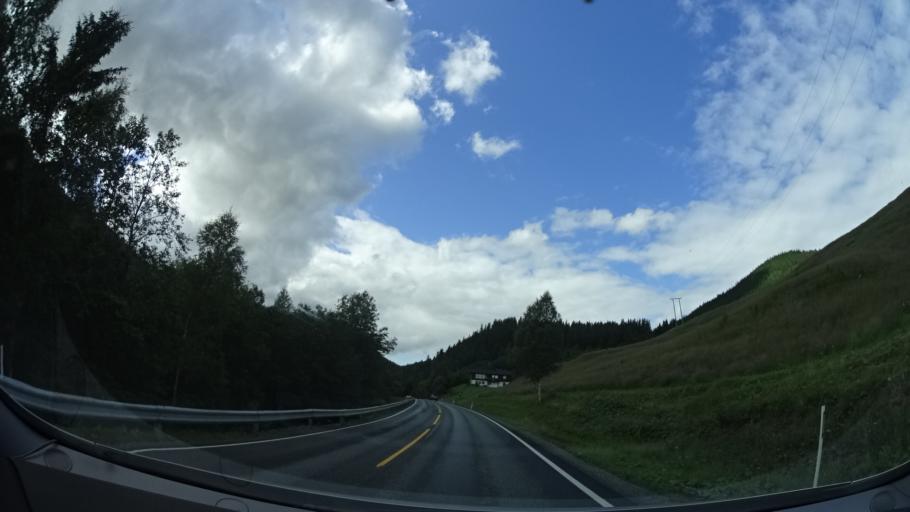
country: NO
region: Nord-Trondelag
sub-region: Meraker
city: Meraker
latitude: 63.4463
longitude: 11.6035
